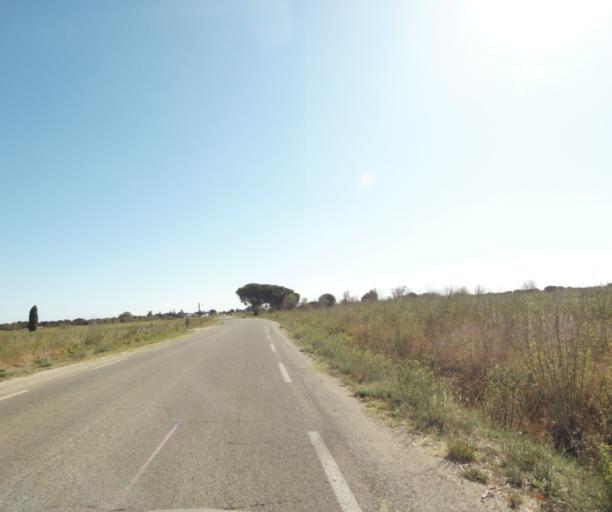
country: FR
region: Languedoc-Roussillon
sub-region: Departement du Gard
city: Manduel
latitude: 43.8120
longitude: 4.4512
